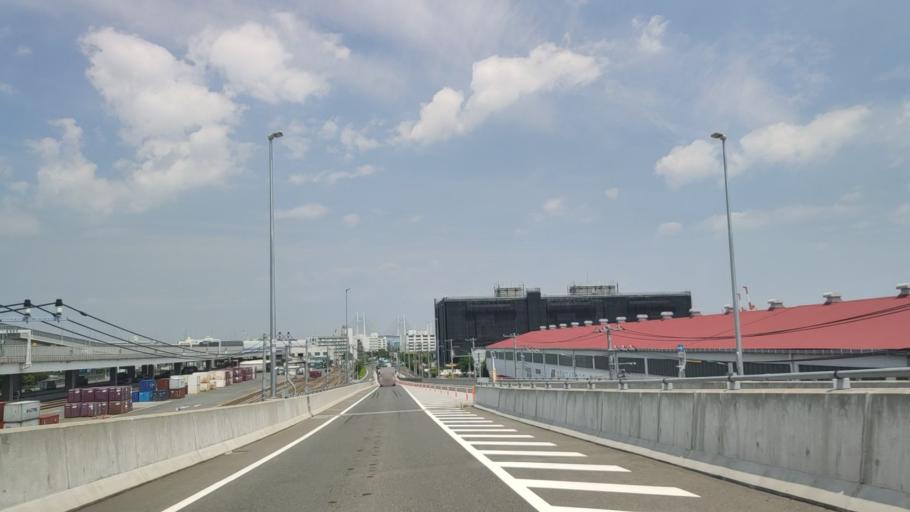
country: JP
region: Kanagawa
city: Yokohama
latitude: 35.4214
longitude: 139.6718
